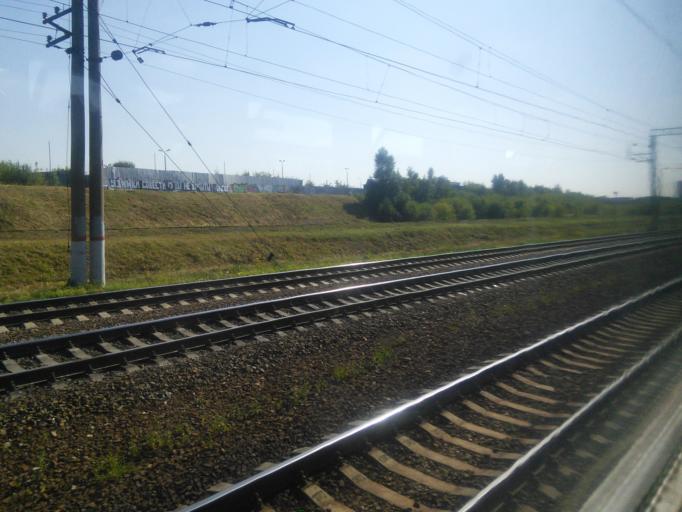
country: RU
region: Moskovskaya
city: Biryulevo Zapadnoye
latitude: 55.5984
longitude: 37.6269
